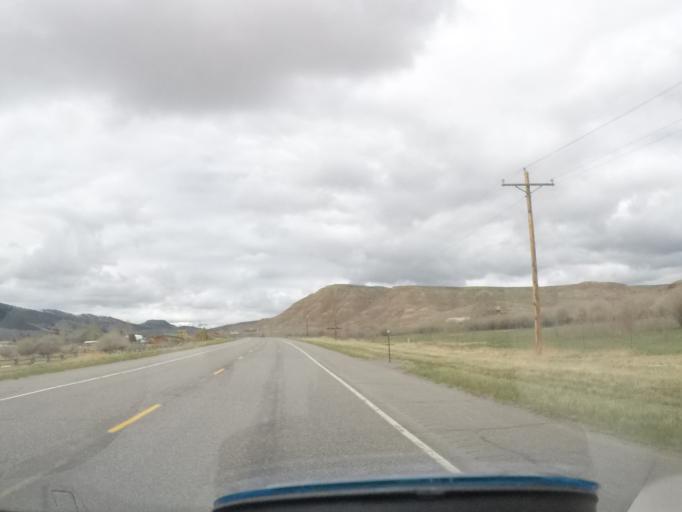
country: US
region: Wyoming
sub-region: Sublette County
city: Pinedale
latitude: 43.5656
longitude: -109.7047
